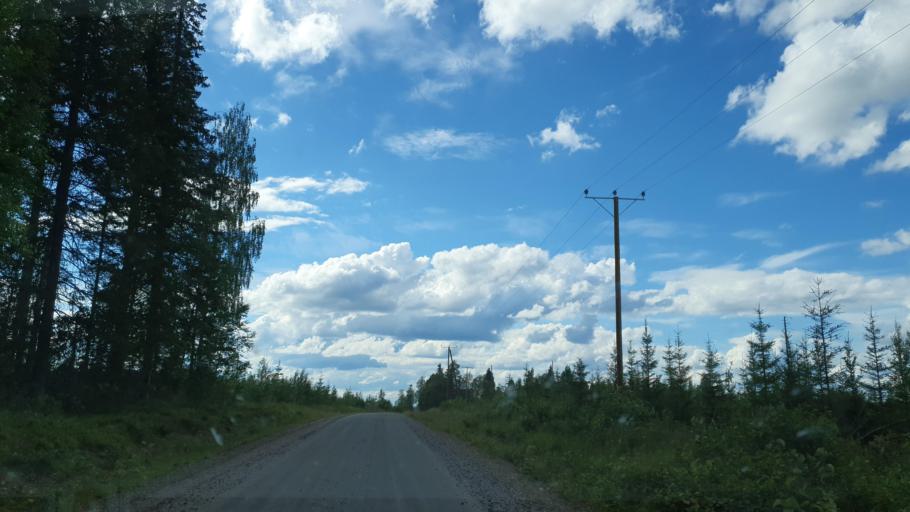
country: FI
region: Kainuu
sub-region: Kehys-Kainuu
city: Kuhmo
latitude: 64.1660
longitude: 29.8789
